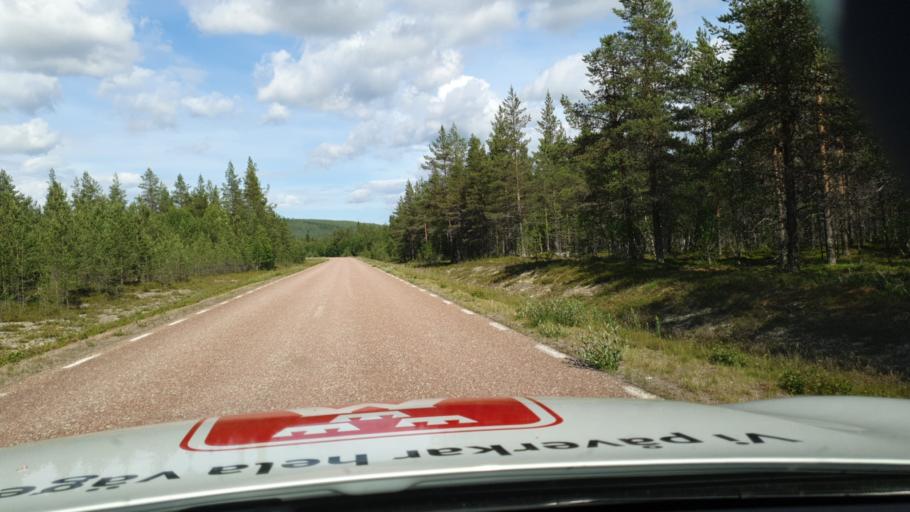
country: SE
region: Dalarna
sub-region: Alvdalens Kommun
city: AElvdalen
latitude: 61.8178
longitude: 13.5521
